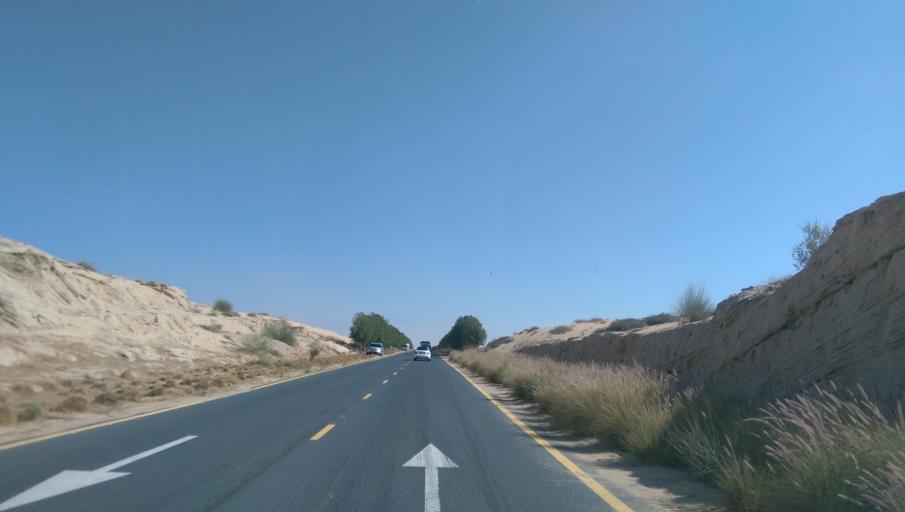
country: AE
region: Dubai
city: Dubai
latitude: 24.9777
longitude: 55.3358
